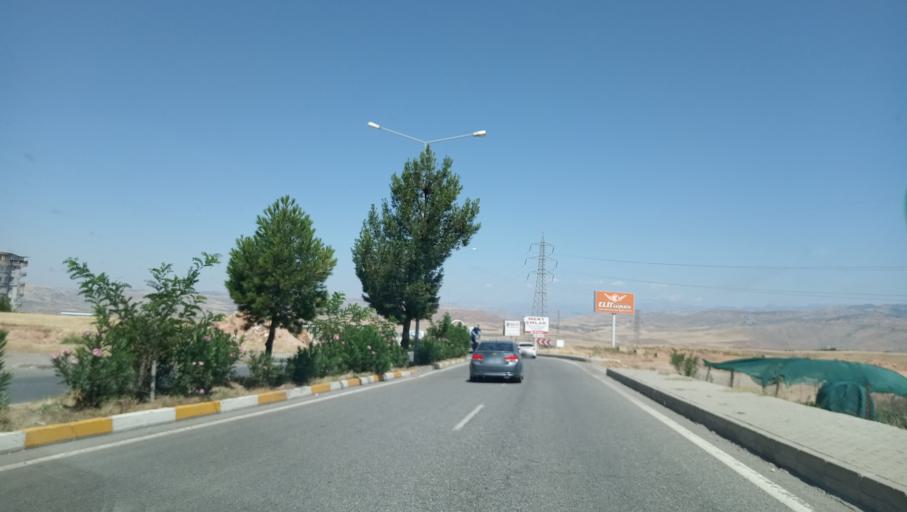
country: TR
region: Siirt
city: Civankan
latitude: 37.9520
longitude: 41.8895
